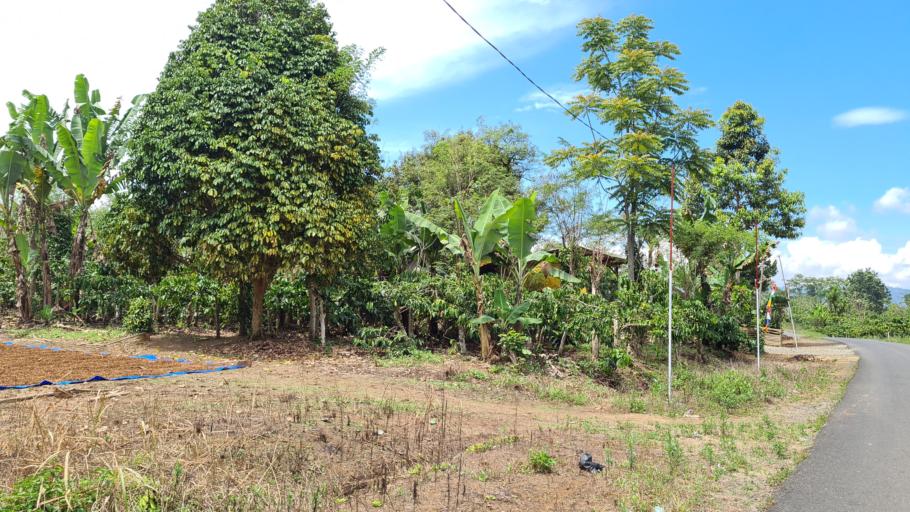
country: ID
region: Lampung
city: Kenali
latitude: -5.0961
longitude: 104.4325
